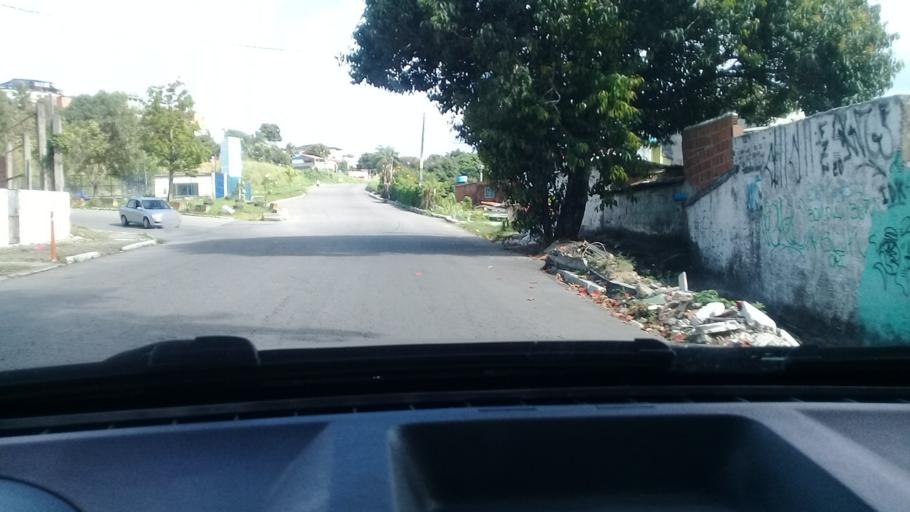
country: BR
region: Pernambuco
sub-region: Jaboatao Dos Guararapes
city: Jaboatao dos Guararapes
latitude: -8.1171
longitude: -34.9428
